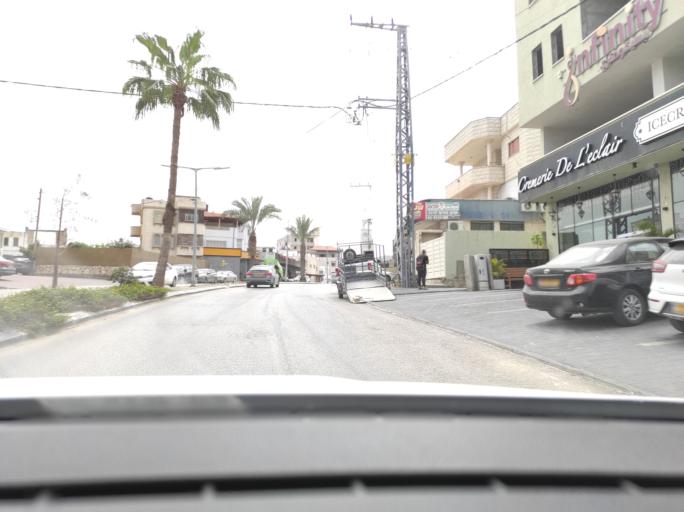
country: IL
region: Central District
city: Kafr Qasim
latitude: 32.1182
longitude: 34.9680
